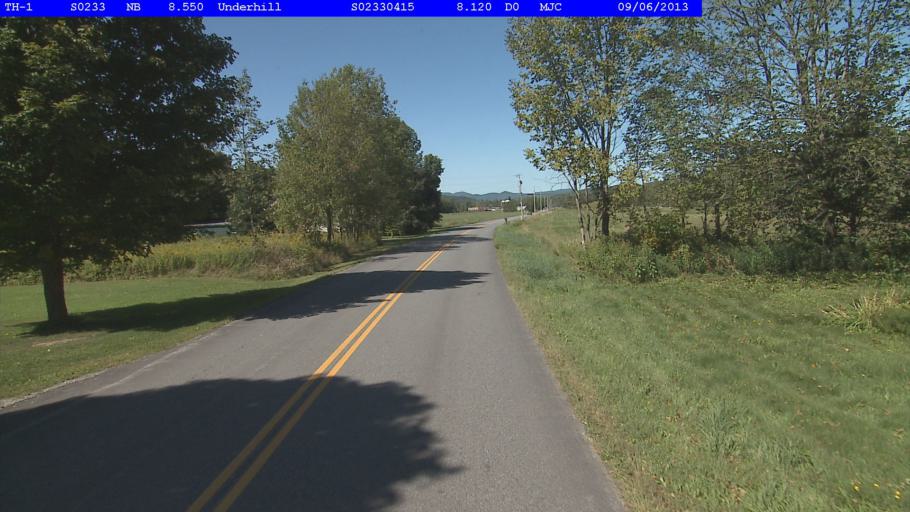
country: US
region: Vermont
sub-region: Chittenden County
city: Jericho
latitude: 44.5816
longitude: -72.8632
